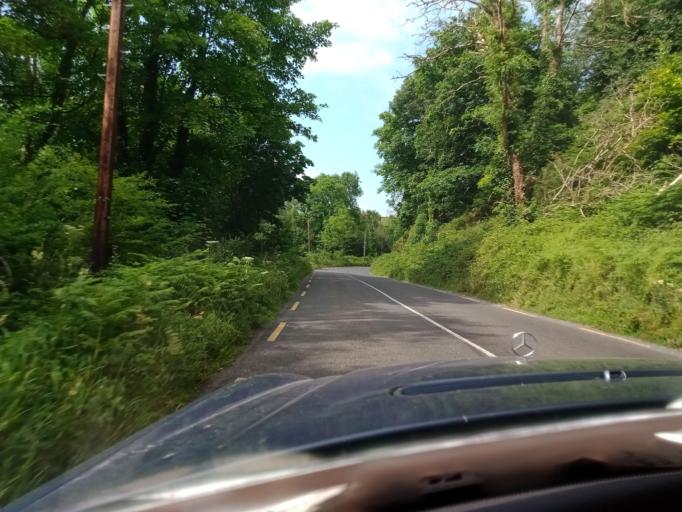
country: IE
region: Munster
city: Carrick-on-Suir
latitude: 52.4185
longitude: -7.3828
